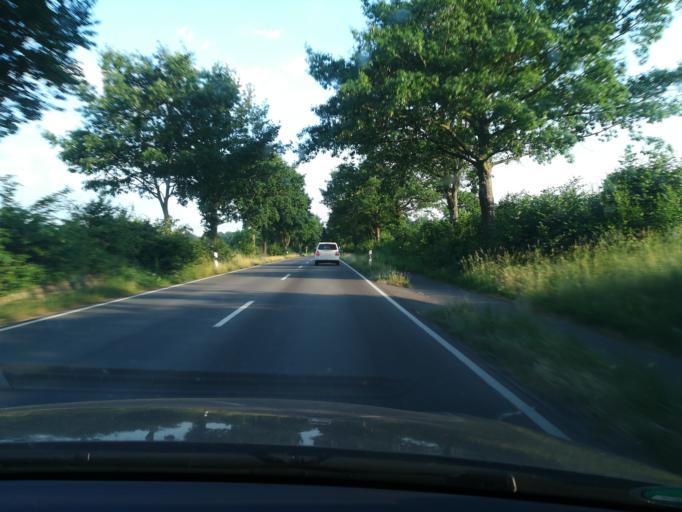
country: DE
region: Schleswig-Holstein
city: Siek
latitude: 53.6296
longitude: 10.3198
